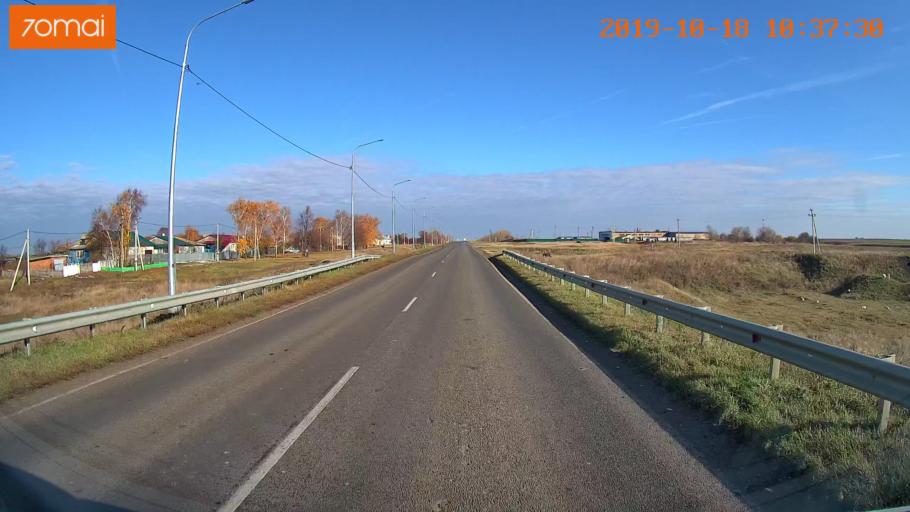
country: RU
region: Tula
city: Kurkino
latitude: 53.5628
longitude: 38.6324
